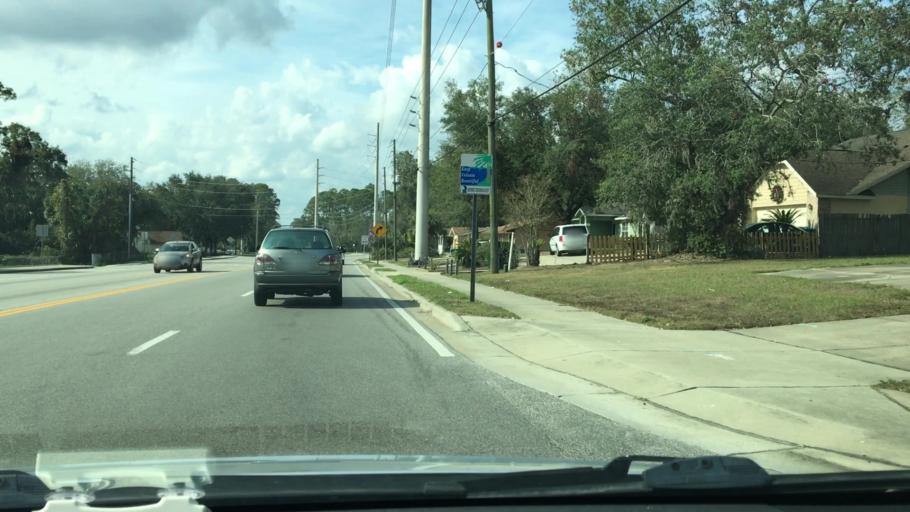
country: US
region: Florida
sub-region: Volusia County
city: Deltona
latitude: 28.8694
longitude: -81.2533
